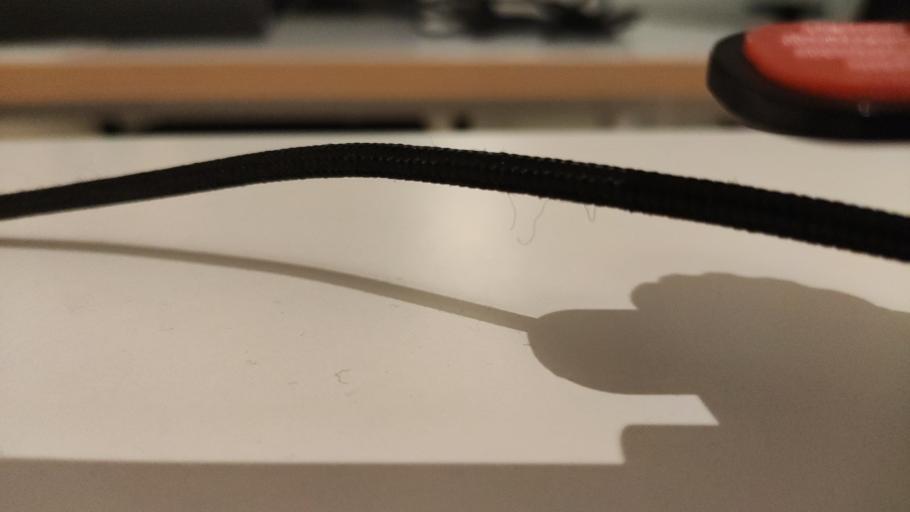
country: RU
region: Moskovskaya
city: Mikhnevo
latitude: 55.0920
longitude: 37.9984
